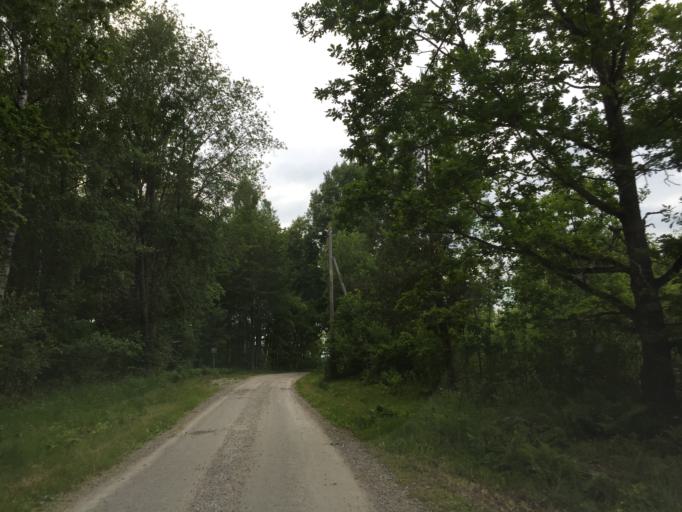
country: SE
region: OErebro
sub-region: Lindesbergs Kommun
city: Fellingsbro
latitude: 59.3242
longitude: 15.5360
